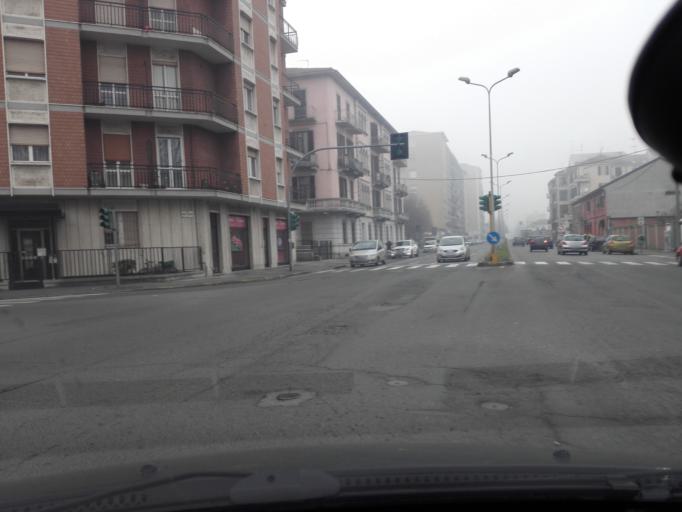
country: IT
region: Piedmont
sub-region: Provincia di Alessandria
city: Alessandria
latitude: 44.9024
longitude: 8.6055
